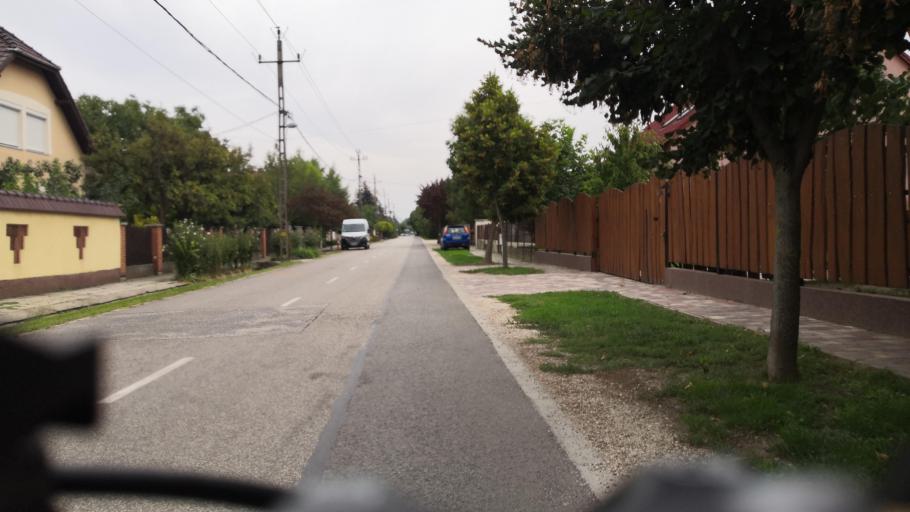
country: HU
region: Csongrad
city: Szeged
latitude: 46.2865
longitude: 20.1645
